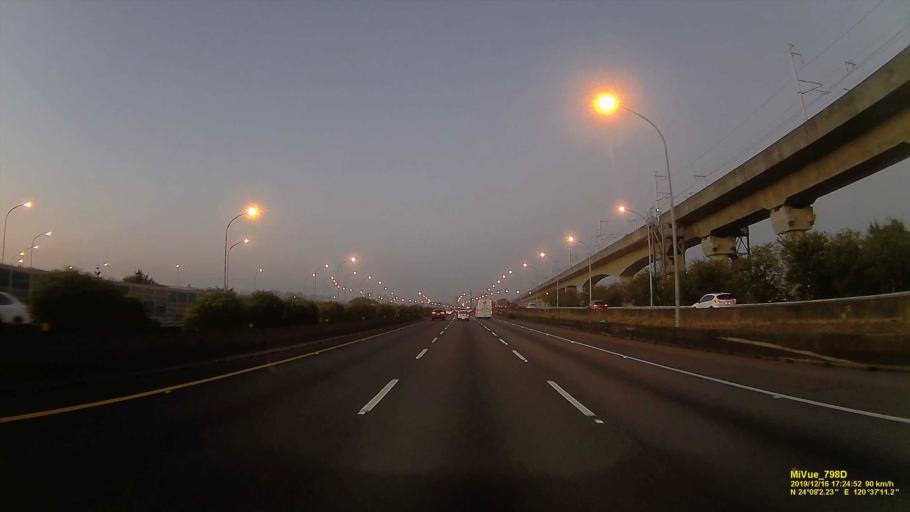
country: TW
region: Taiwan
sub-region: Taichung City
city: Taichung
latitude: 24.1506
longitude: 120.6198
